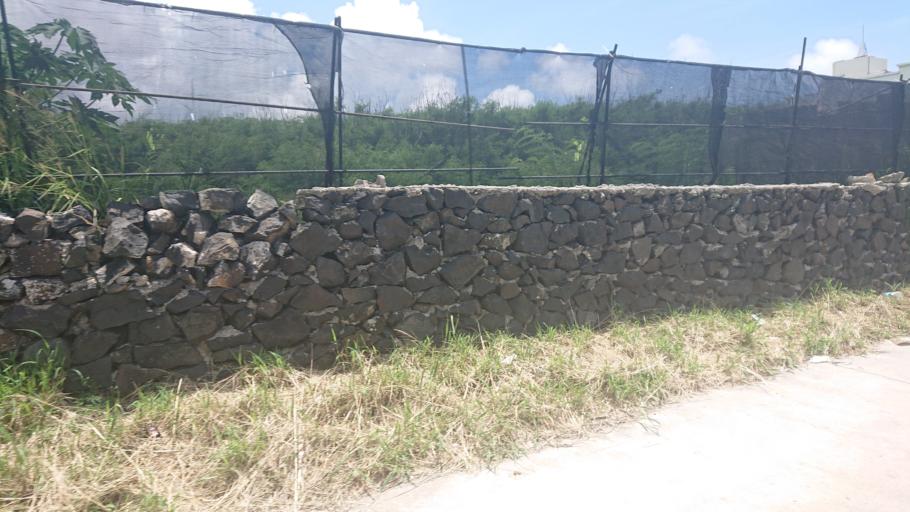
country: TW
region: Taiwan
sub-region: Penghu
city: Ma-kung
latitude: 23.5769
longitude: 119.5786
